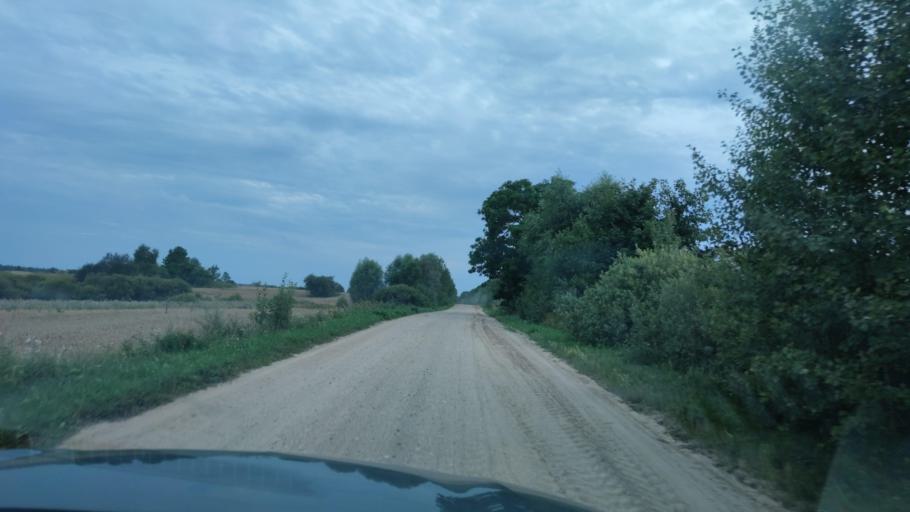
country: BY
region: Minsk
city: Myadzyel
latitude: 55.0953
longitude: 27.1344
